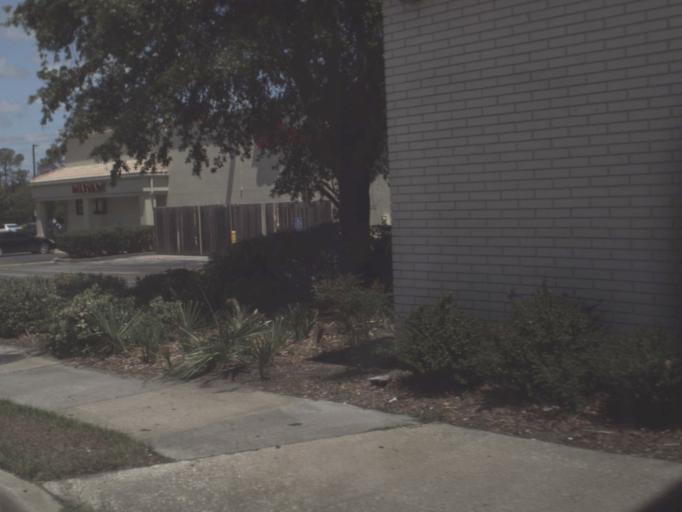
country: US
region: Florida
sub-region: Marion County
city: Ocala
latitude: 29.1871
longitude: -82.1286
